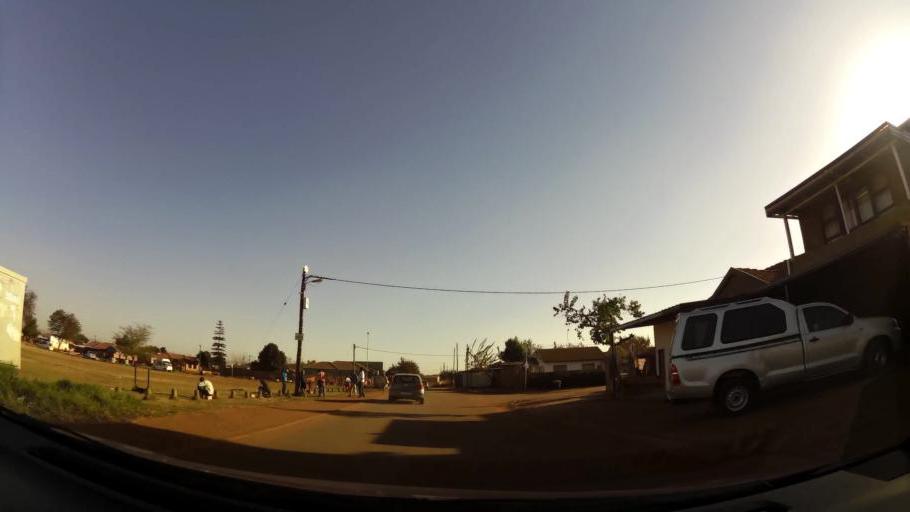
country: ZA
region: Gauteng
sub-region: City of Tshwane Metropolitan Municipality
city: Mabopane
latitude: -25.5909
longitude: 28.0975
